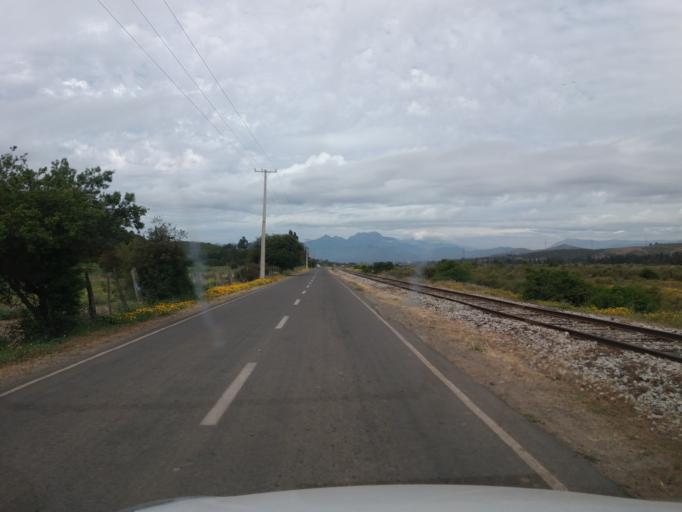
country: CL
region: Valparaiso
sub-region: Provincia de Marga Marga
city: Quilpue
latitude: -32.9161
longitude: -71.4227
